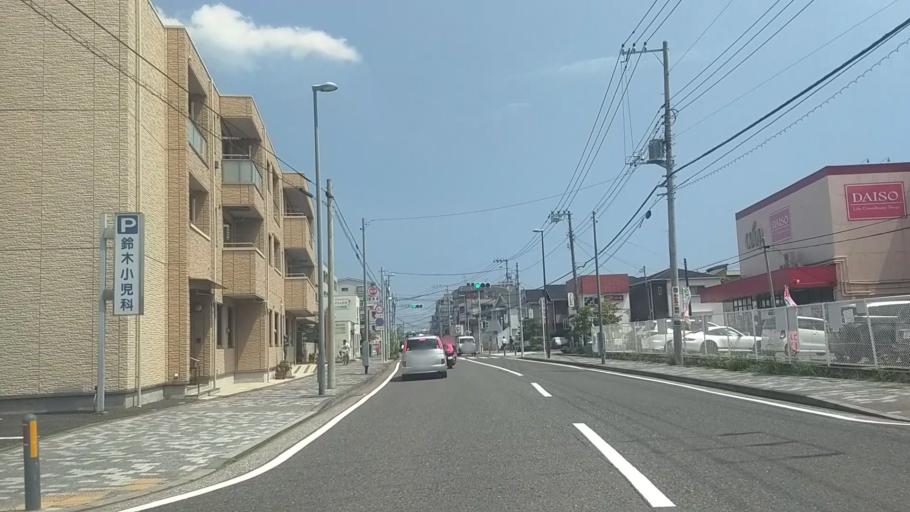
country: JP
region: Kanagawa
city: Yokohama
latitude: 35.4870
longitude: 139.6140
